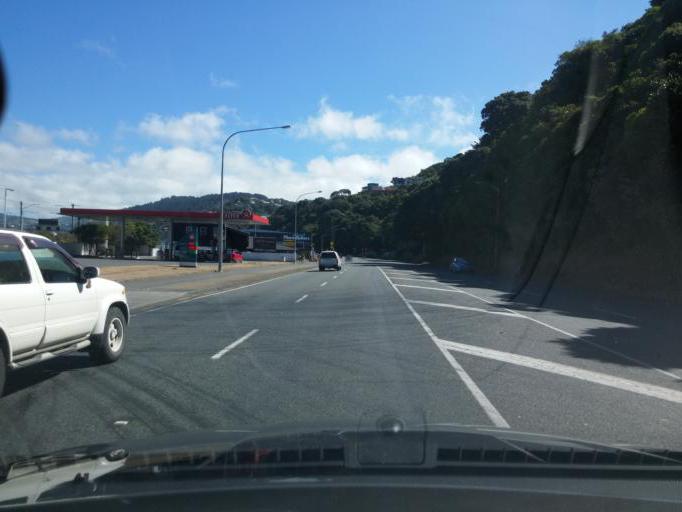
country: NZ
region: Wellington
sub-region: Wellington City
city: Wellington
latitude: -41.2550
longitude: 174.7990
